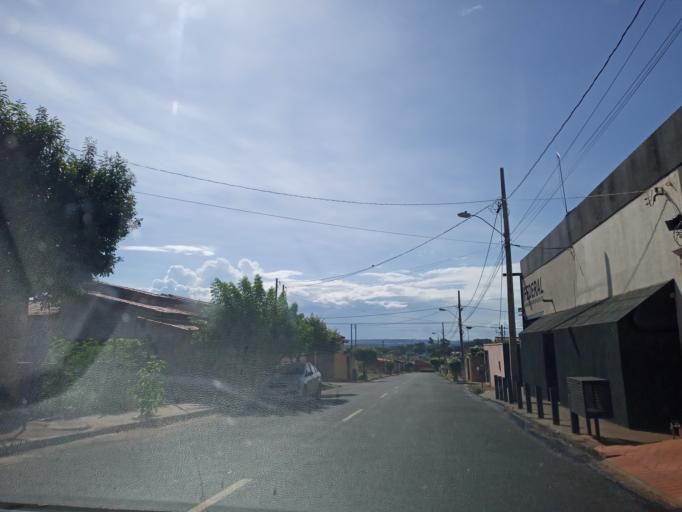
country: BR
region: Goias
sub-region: Itumbiara
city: Itumbiara
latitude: -18.4387
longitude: -49.1815
